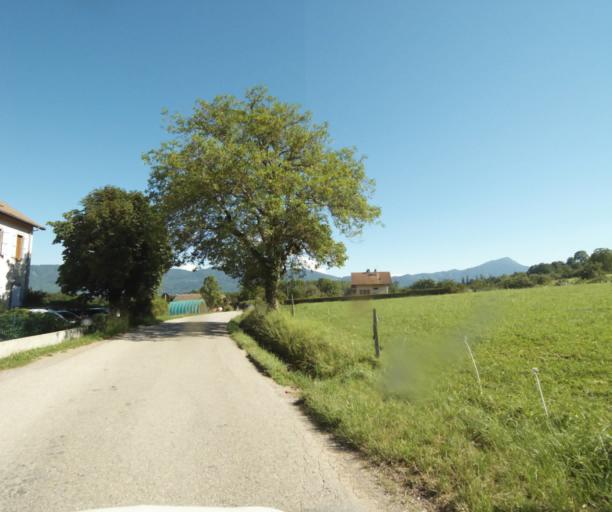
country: FR
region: Rhone-Alpes
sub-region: Departement de la Haute-Savoie
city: Sciez
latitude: 46.3139
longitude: 6.3815
